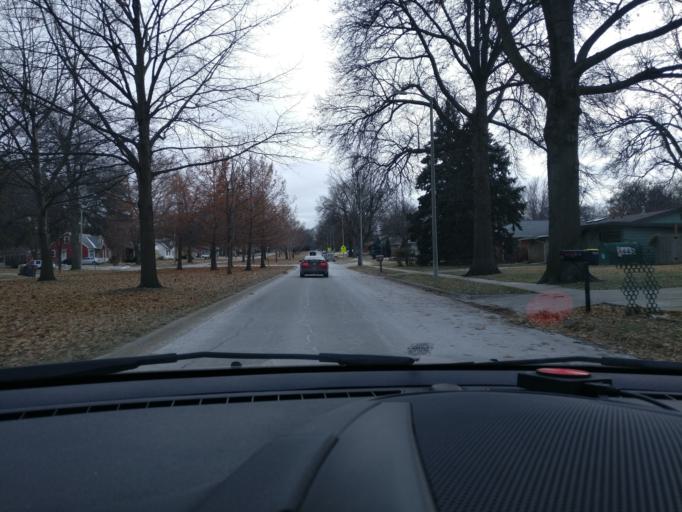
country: US
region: Nebraska
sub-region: Lancaster County
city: Lincoln
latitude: 40.8473
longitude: -96.6402
